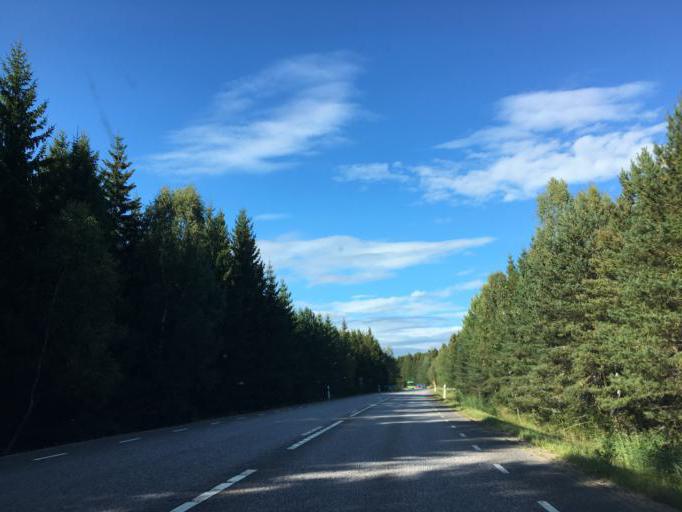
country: SE
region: Soedermanland
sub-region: Nykopings Kommun
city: Svalsta
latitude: 58.8451
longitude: 16.9218
